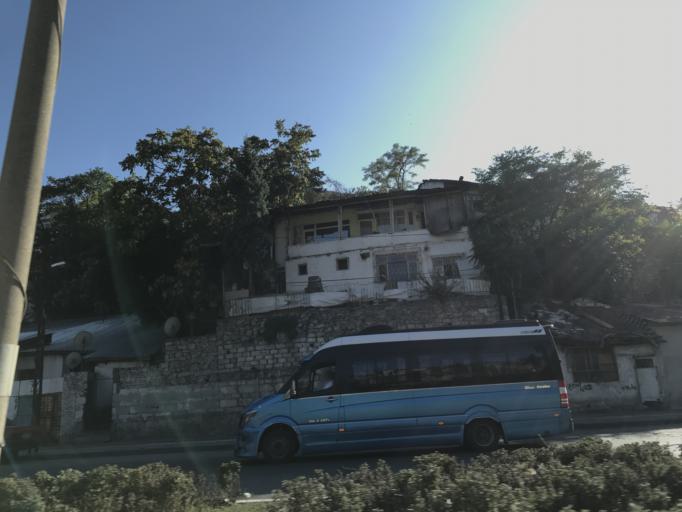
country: TR
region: Ankara
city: Cankaya
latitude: 39.9422
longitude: 32.8704
